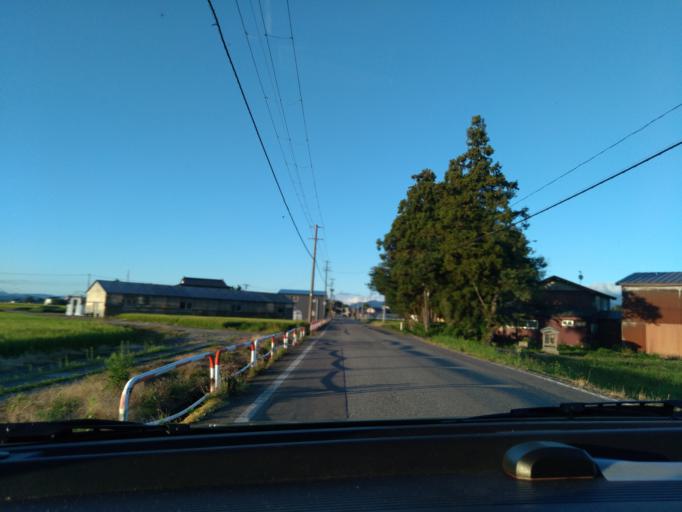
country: JP
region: Akita
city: Omagari
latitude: 39.4769
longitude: 140.5213
